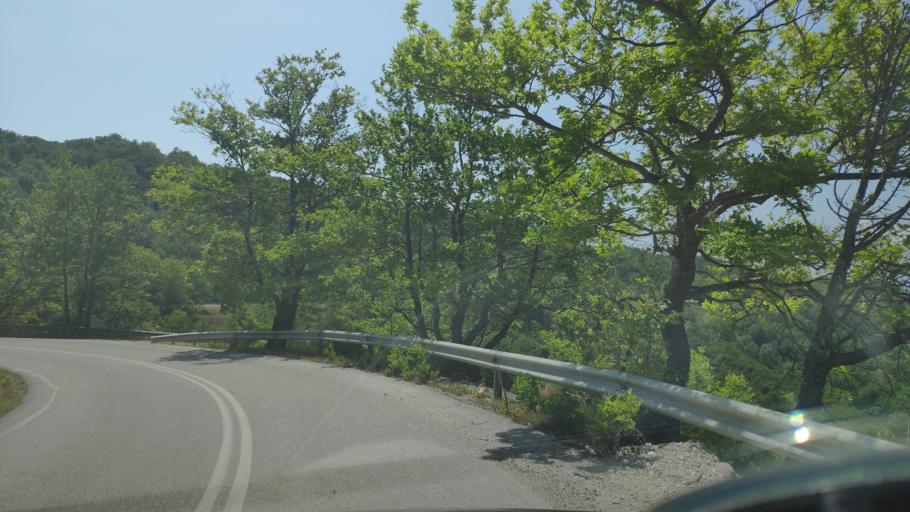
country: GR
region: Epirus
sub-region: Nomos Artas
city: Ano Kalentini
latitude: 39.2398
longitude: 21.2015
